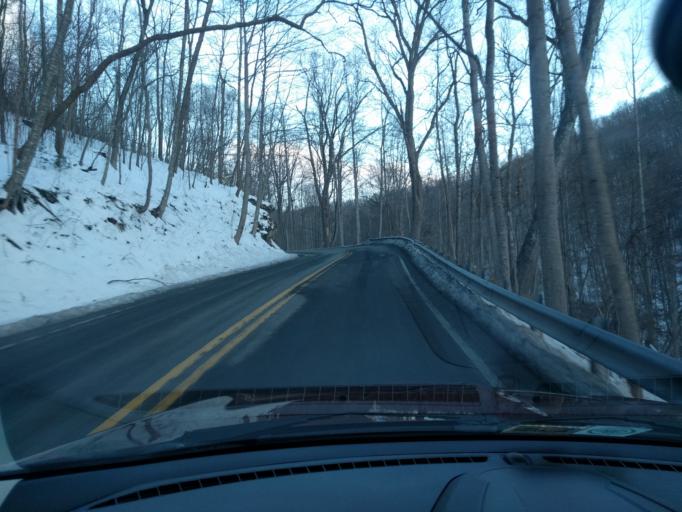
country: US
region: Virginia
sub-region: Bath County
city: Warm Springs
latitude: 38.0940
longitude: -79.8410
